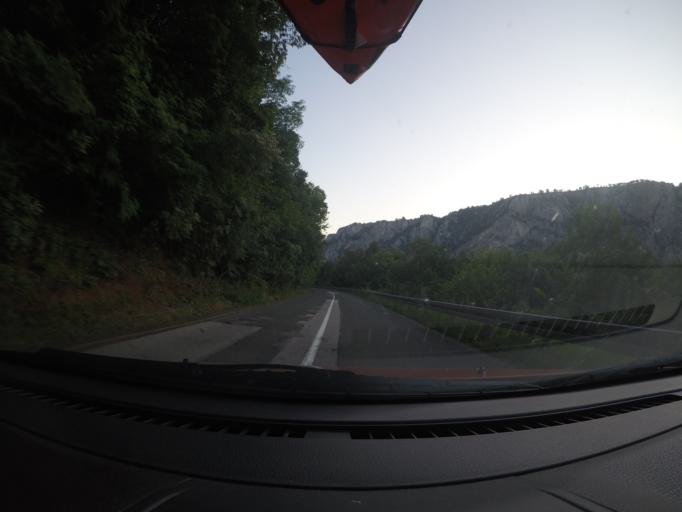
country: RO
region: Mehedinti
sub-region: Comuna Dubova
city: Dubova
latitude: 44.5999
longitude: 22.2709
